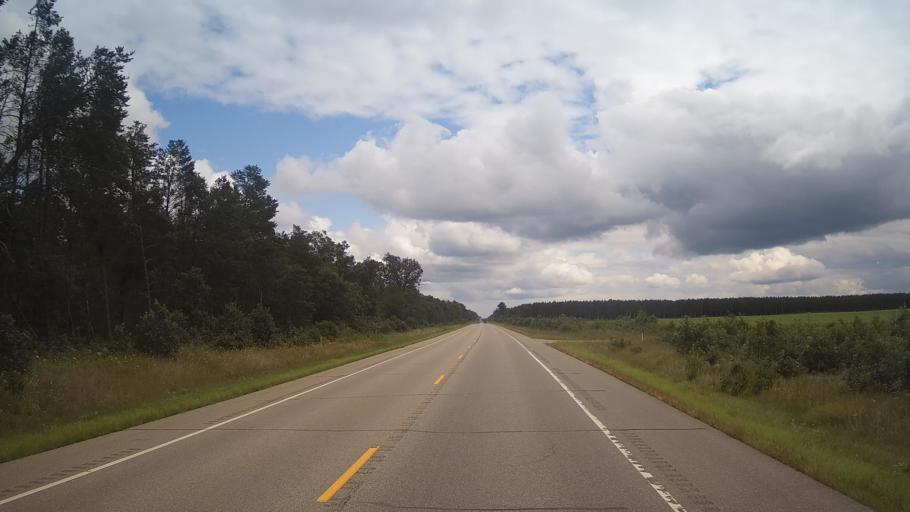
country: US
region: Wisconsin
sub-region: Adams County
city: Friendship
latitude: 44.0250
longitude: -89.7590
